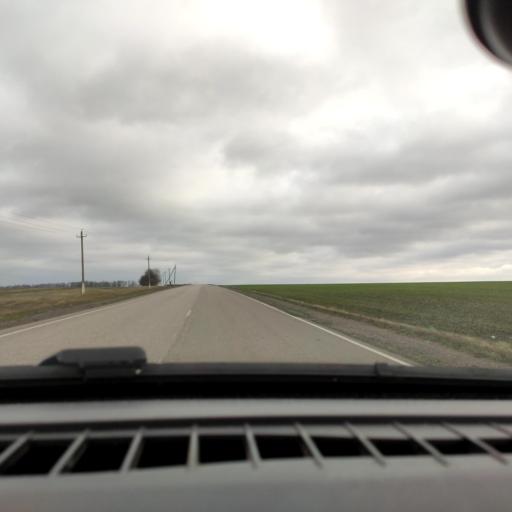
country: RU
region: Belgorod
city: Ilovka
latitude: 50.7712
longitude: 38.7724
